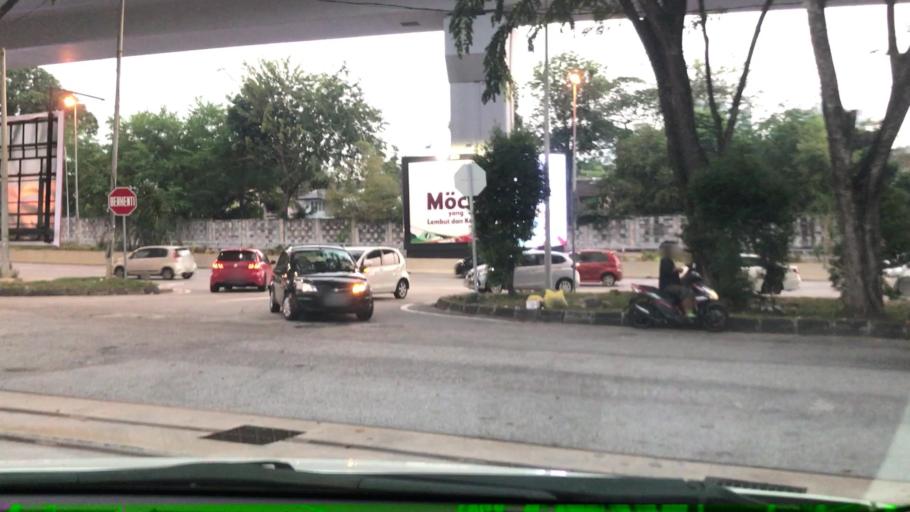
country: MY
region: Selangor
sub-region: Petaling
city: Petaling Jaya
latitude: 3.1419
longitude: 101.6258
